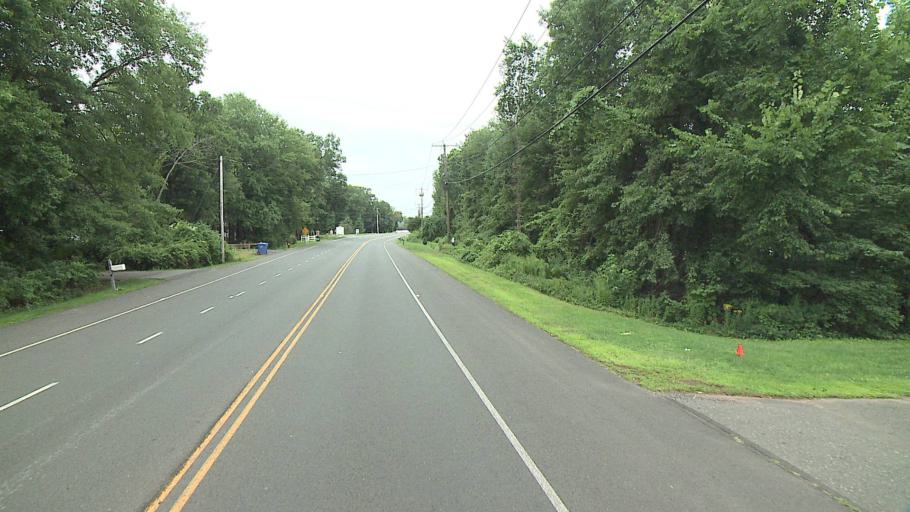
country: US
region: Connecticut
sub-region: Middlesex County
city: Cromwell
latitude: 41.6109
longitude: -72.6760
